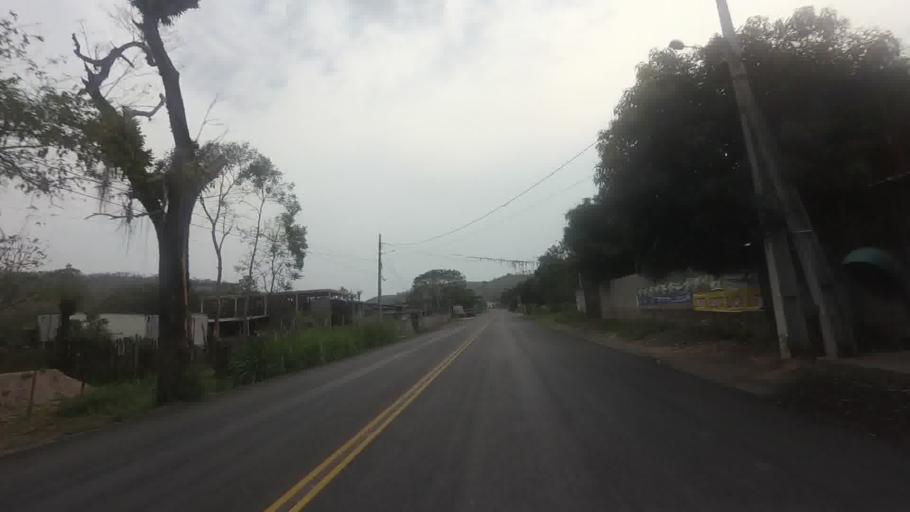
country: BR
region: Rio de Janeiro
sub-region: Santo Antonio De Padua
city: Santo Antonio de Padua
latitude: -21.5341
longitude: -42.1520
